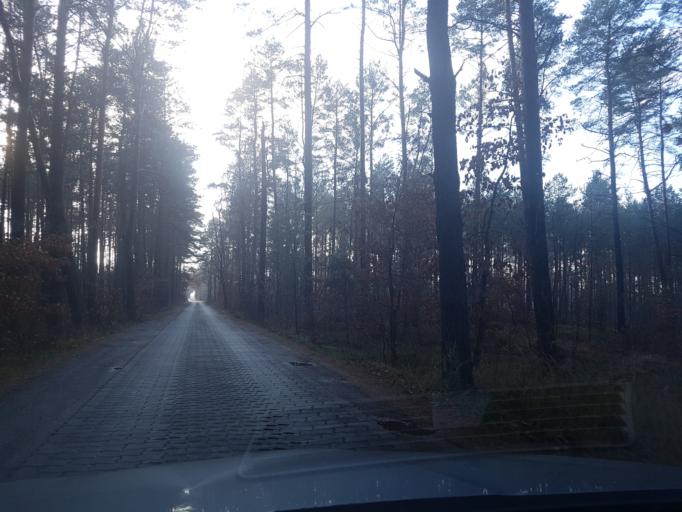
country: DE
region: Brandenburg
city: Ruckersdorf
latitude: 51.5442
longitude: 13.6074
